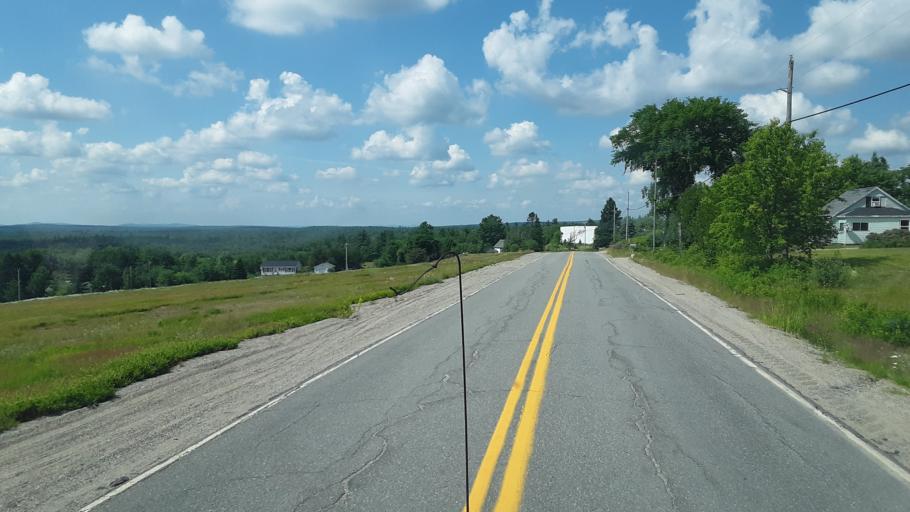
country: US
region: Maine
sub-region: Washington County
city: Machias
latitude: 44.9493
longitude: -67.6639
